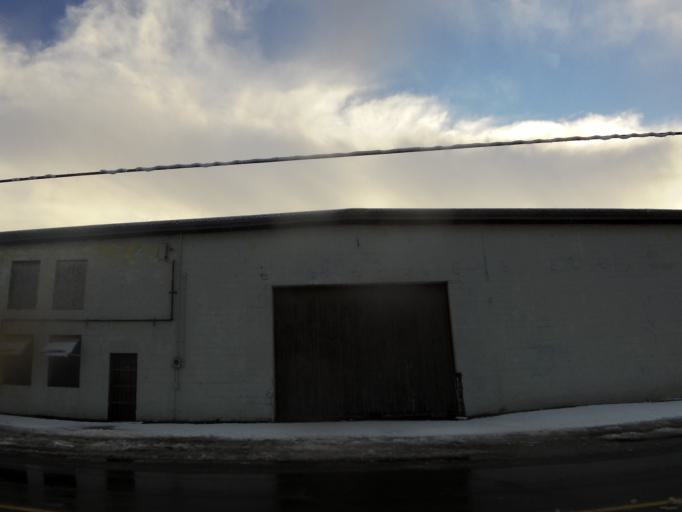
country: US
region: North Carolina
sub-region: Nash County
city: Rocky Mount
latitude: 35.9246
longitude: -77.8045
